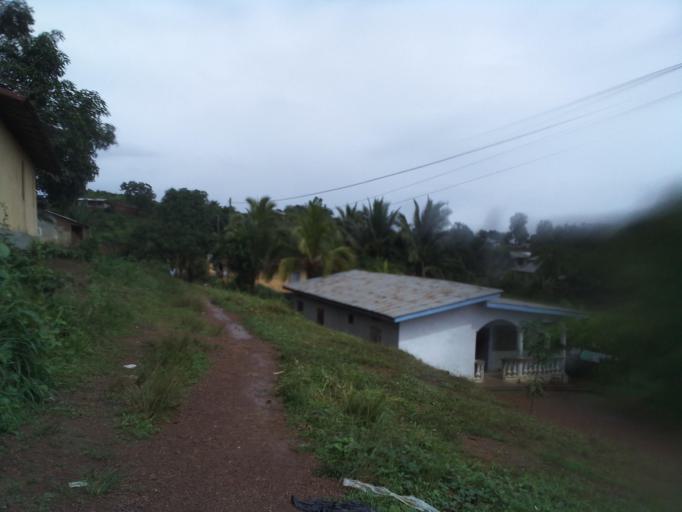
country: SL
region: Eastern Province
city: Kenema
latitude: 7.8487
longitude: -11.1945
